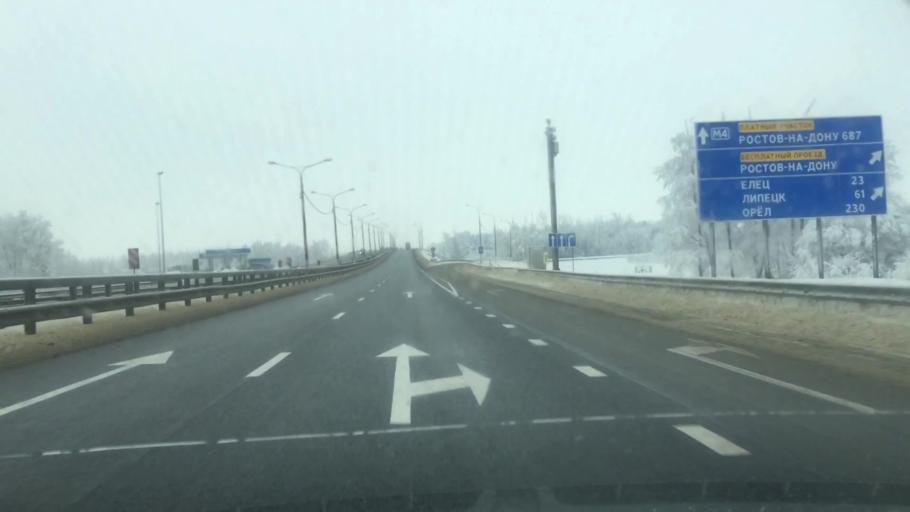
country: RU
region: Lipetsk
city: Yelets
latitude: 52.5529
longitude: 38.7165
